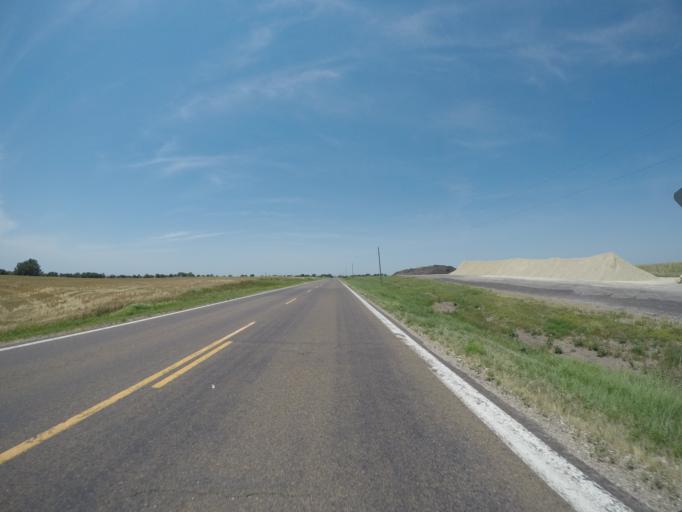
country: US
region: Kansas
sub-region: Geary County
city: Junction City
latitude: 39.0302
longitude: -96.8928
